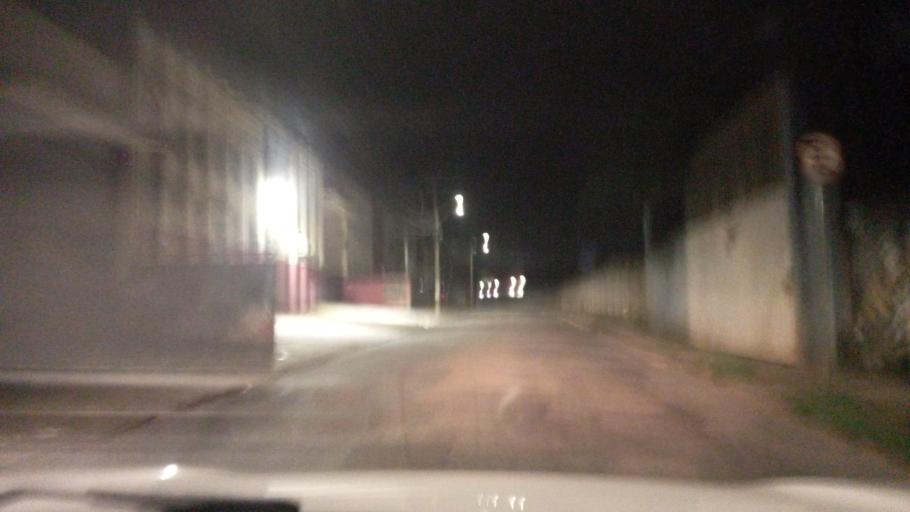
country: BR
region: Minas Gerais
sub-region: Belo Horizonte
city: Belo Horizonte
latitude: -19.8947
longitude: -43.9614
